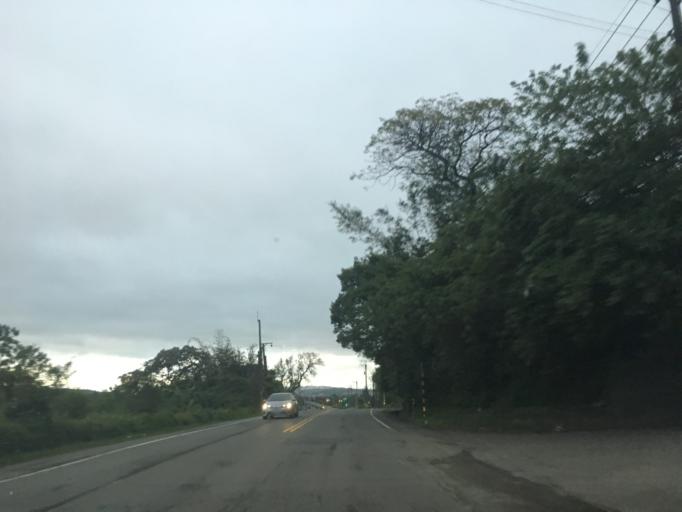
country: TW
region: Taiwan
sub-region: Miaoli
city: Miaoli
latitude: 24.4549
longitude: 120.7810
